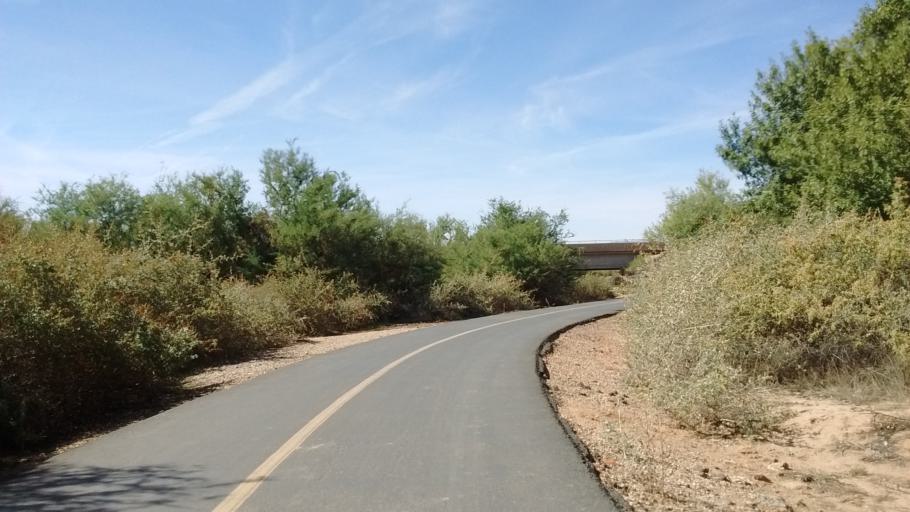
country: US
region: Utah
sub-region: Washington County
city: Saint George
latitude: 37.0870
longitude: -113.5554
